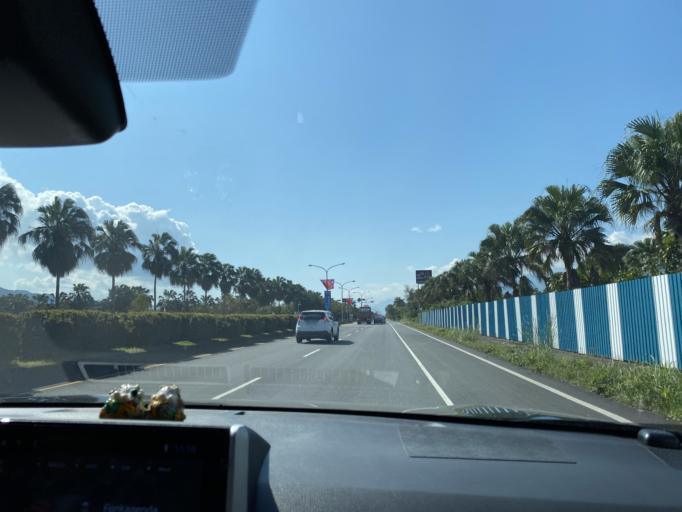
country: TW
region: Taiwan
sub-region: Hualien
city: Hualian
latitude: 23.8648
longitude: 121.5312
